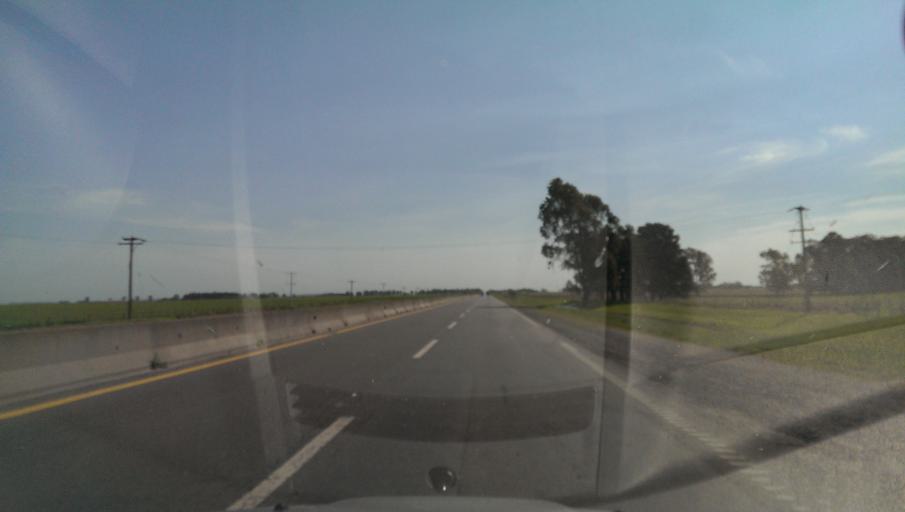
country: AR
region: Buenos Aires
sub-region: Partido de Azul
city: Azul
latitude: -36.8447
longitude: -59.9188
